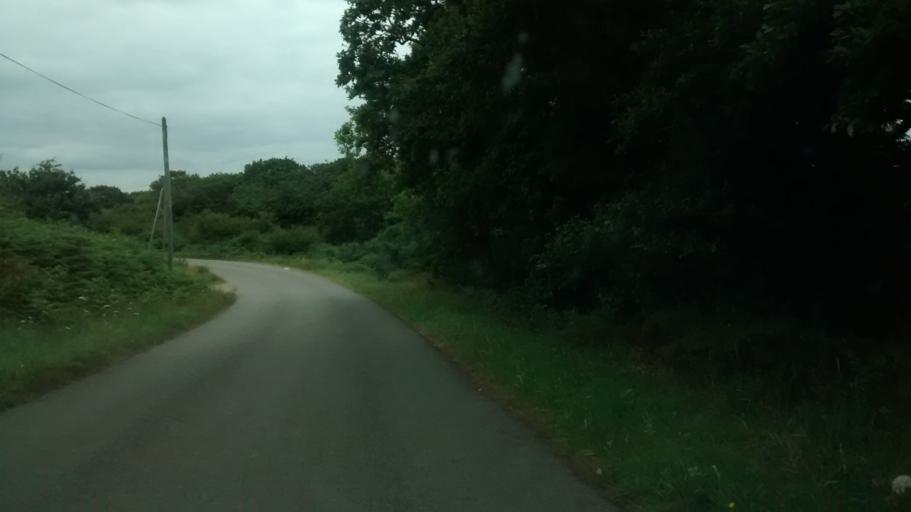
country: FR
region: Brittany
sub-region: Departement du Finistere
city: Plougastel-Daoulas
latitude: 48.3342
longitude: -4.4003
